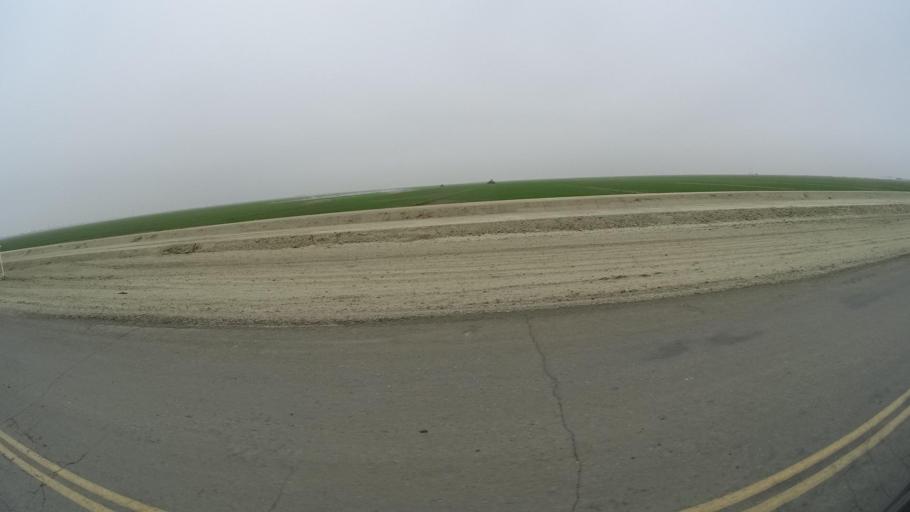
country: US
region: California
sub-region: Kern County
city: Rosedale
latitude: 35.2101
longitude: -119.2259
